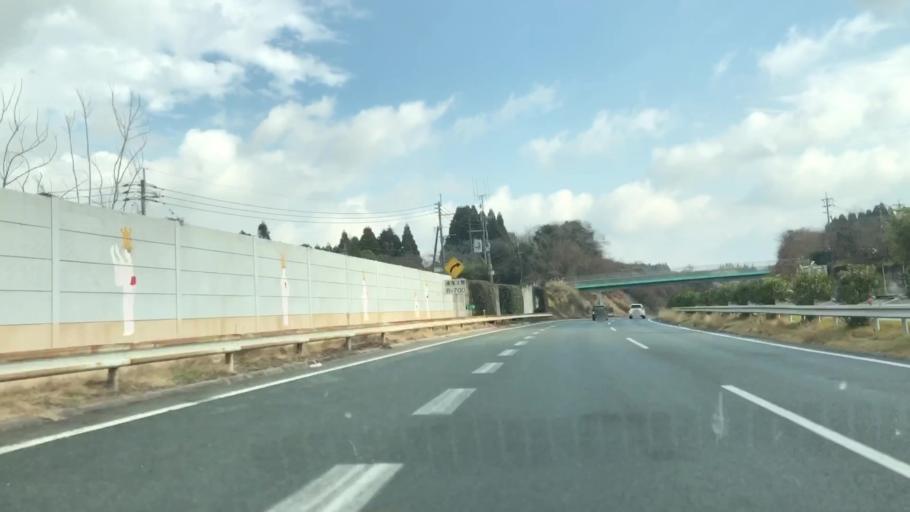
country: JP
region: Fukuoka
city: Omuta
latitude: 33.0435
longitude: 130.5652
